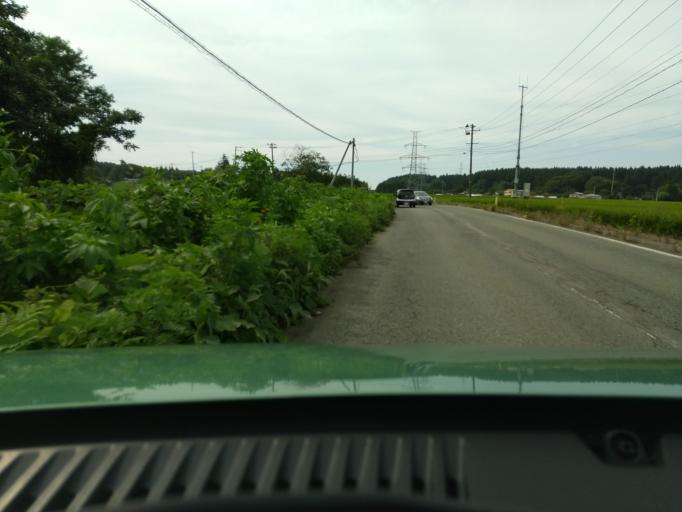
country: JP
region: Akita
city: Akita
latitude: 39.7890
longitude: 140.1193
